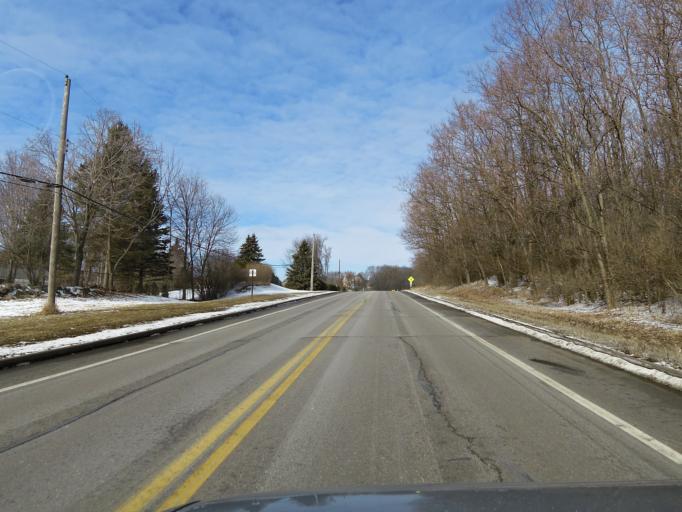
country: US
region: Minnesota
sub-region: Scott County
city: Savage
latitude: 44.8218
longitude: -93.3788
